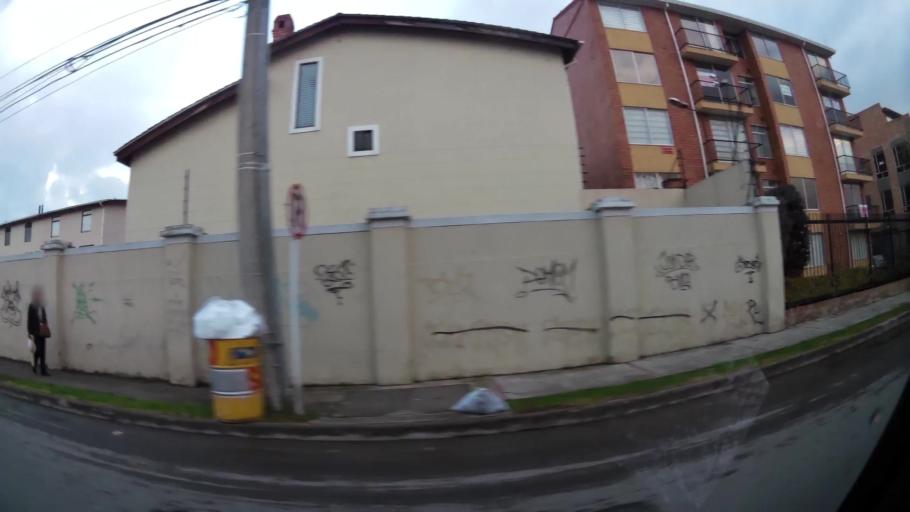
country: CO
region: Cundinamarca
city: Chia
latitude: 4.8519
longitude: -74.0576
